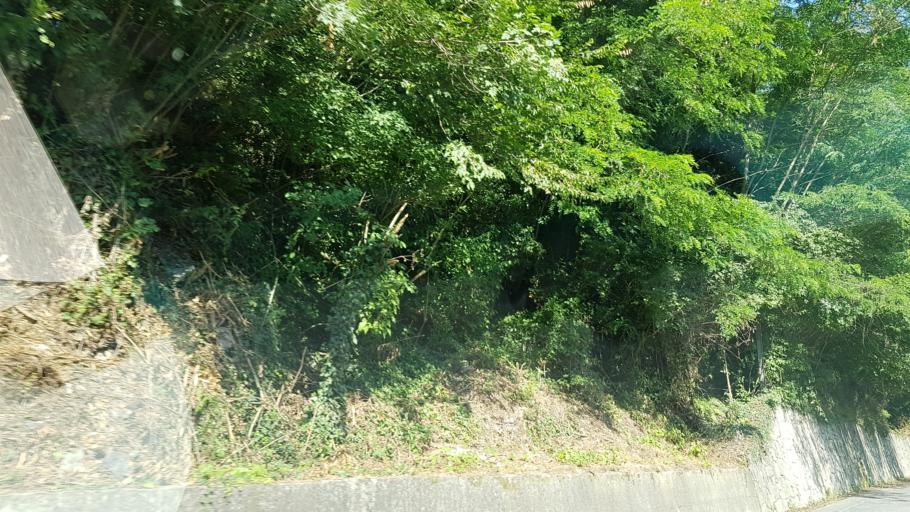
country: IT
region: Liguria
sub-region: Provincia di Genova
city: Serra Ricco
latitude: 44.5143
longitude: 8.9401
